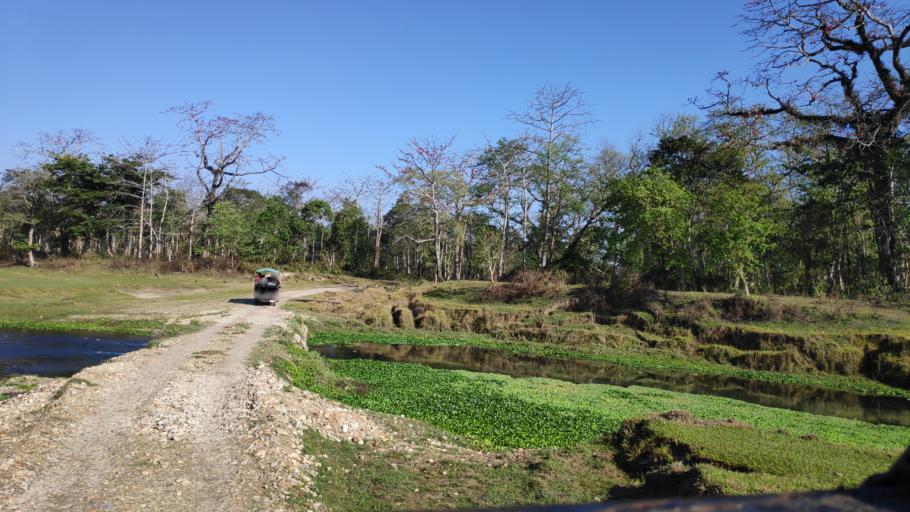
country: NP
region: Central Region
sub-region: Narayani Zone
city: Bharatpur
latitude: 27.5623
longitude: 84.5221
